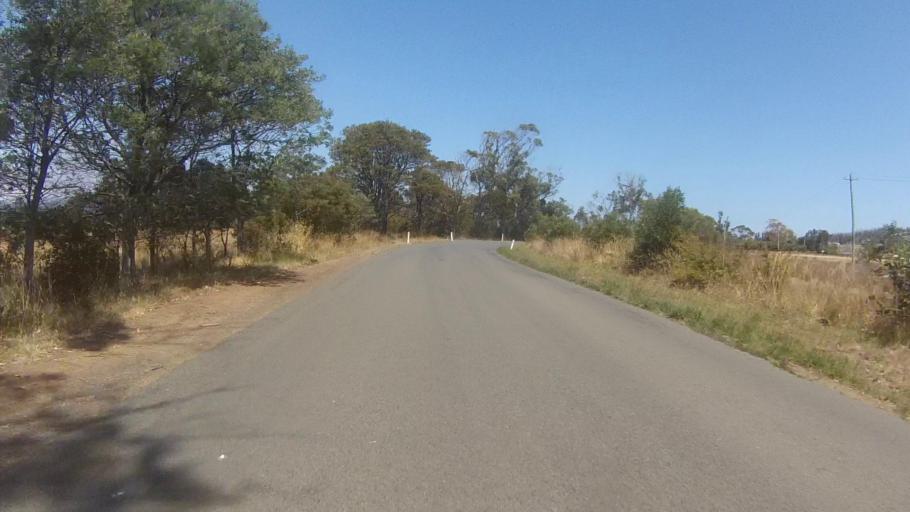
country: AU
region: Tasmania
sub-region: Sorell
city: Sorell
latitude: -42.8628
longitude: 147.8338
